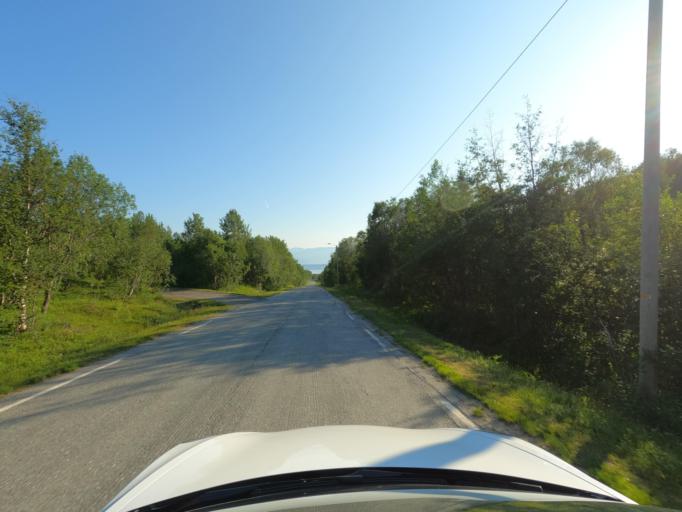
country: NO
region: Nordland
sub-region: Narvik
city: Bjerkvik
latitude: 68.5396
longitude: 17.4888
